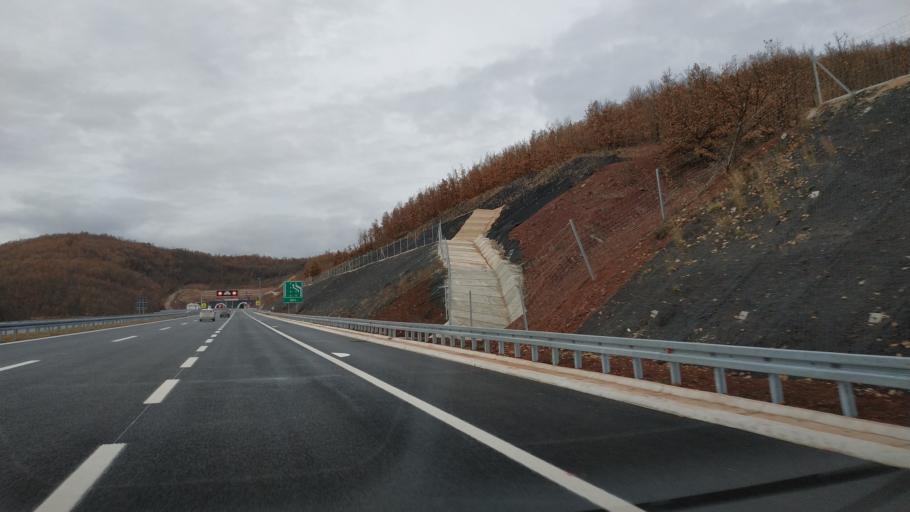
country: RS
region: Central Serbia
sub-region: Nisavski Okrug
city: Gadzin Han
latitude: 43.2623
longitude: 22.1447
